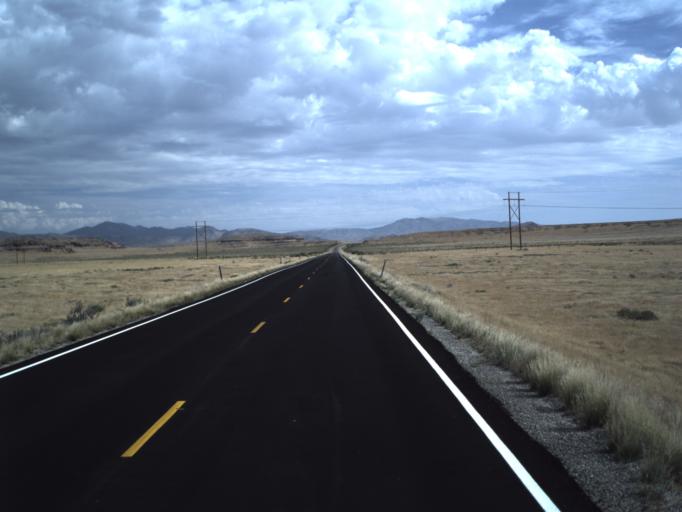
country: US
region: Utah
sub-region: Tooele County
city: Wendover
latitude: 41.4120
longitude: -113.9257
